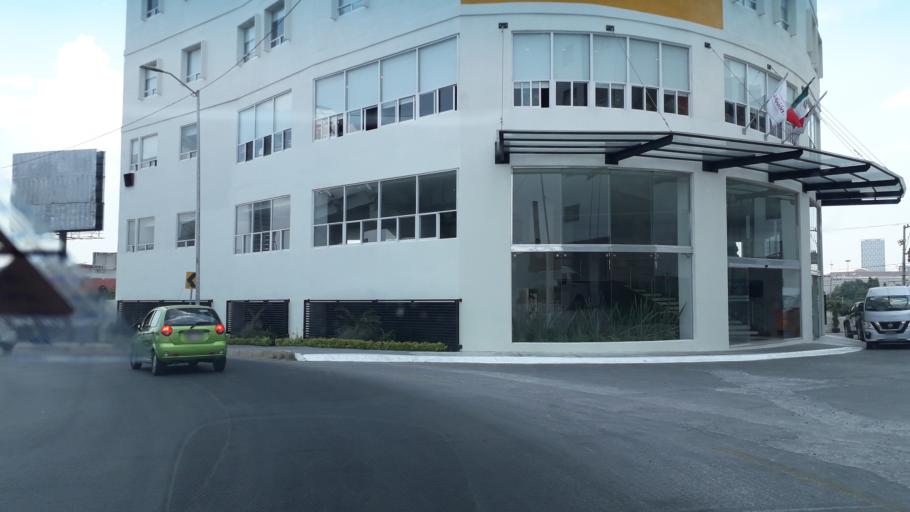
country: MX
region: Puebla
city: Puebla
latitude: 19.0377
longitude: -98.2266
